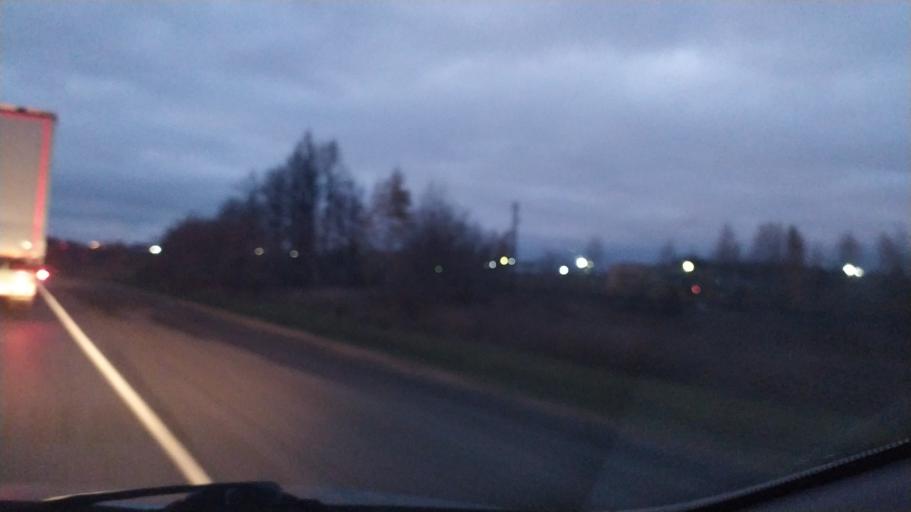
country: RU
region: Chuvashia
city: Kugesi
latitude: 56.0589
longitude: 47.2590
